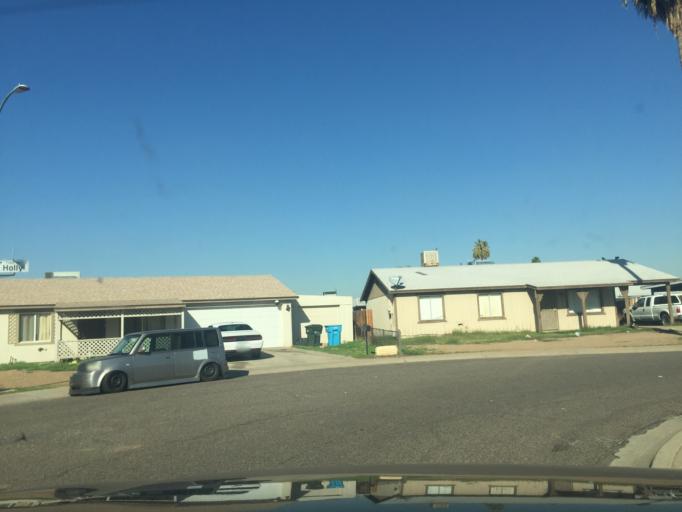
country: US
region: Arizona
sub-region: Maricopa County
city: Tolleson
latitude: 33.4697
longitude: -112.2146
